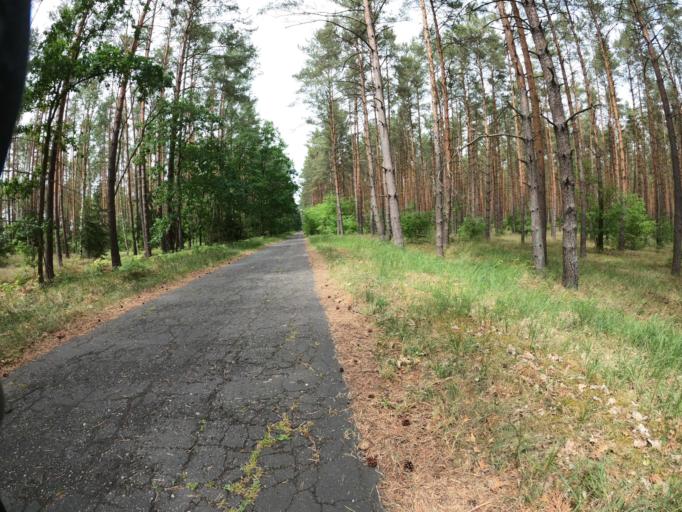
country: PL
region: West Pomeranian Voivodeship
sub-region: Powiat mysliborski
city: Boleszkowice
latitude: 52.7097
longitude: 14.5034
